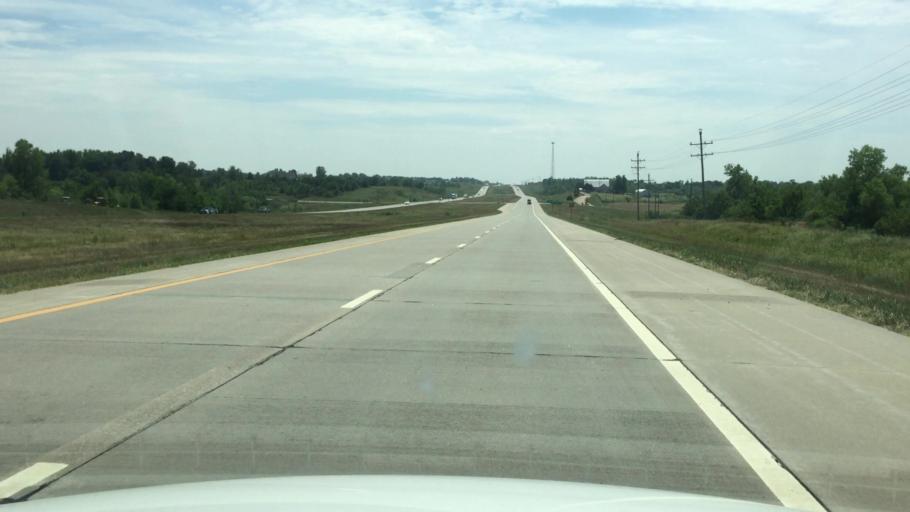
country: US
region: Kansas
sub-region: Jackson County
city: Holton
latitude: 39.2641
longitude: -95.7201
